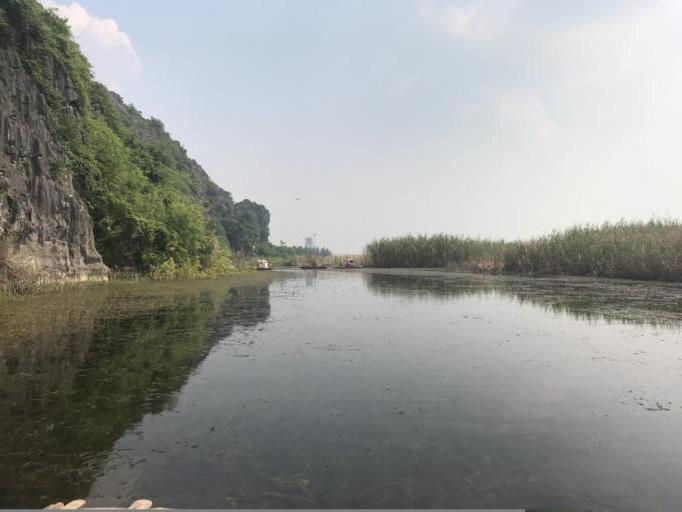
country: VN
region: Ninh Binh
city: Thi Tran Me
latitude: 20.3634
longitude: 105.8890
